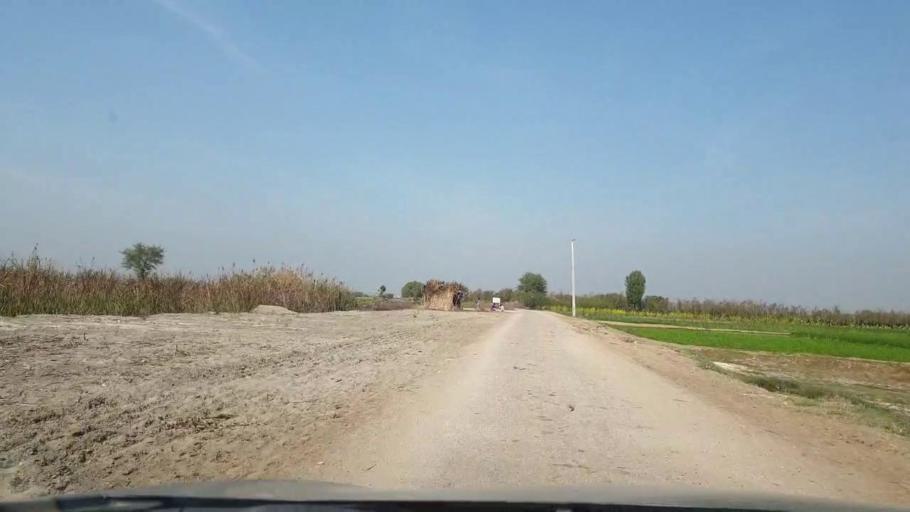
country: PK
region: Sindh
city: Berani
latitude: 25.6978
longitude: 68.7536
